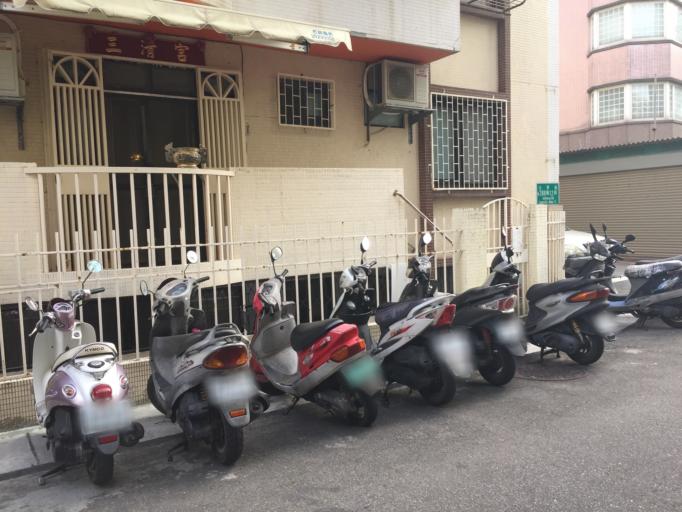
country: TW
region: Taipei
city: Taipei
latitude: 25.1118
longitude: 121.5360
